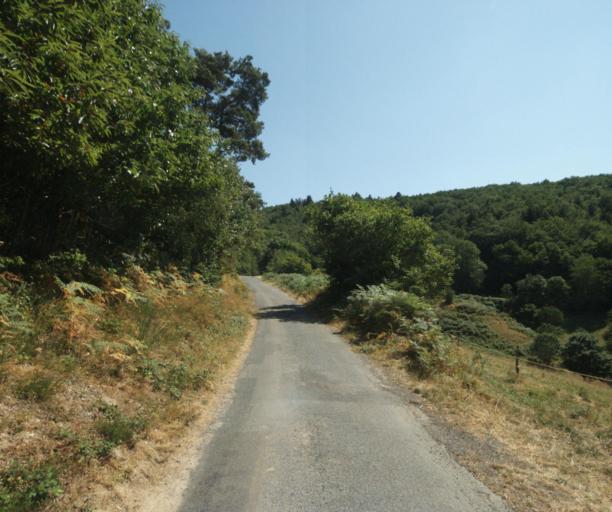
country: FR
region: Rhone-Alpes
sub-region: Departement du Rhone
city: Courzieu
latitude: 45.7194
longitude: 4.5481
